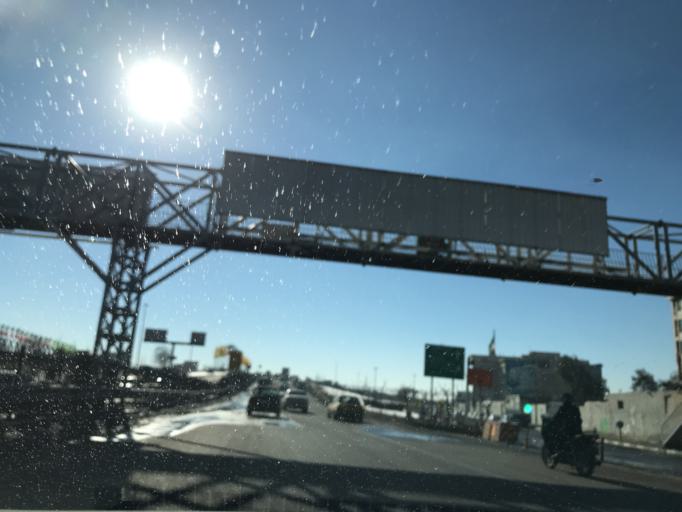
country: IR
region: Tehran
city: Tehran
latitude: 35.6381
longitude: 51.3589
